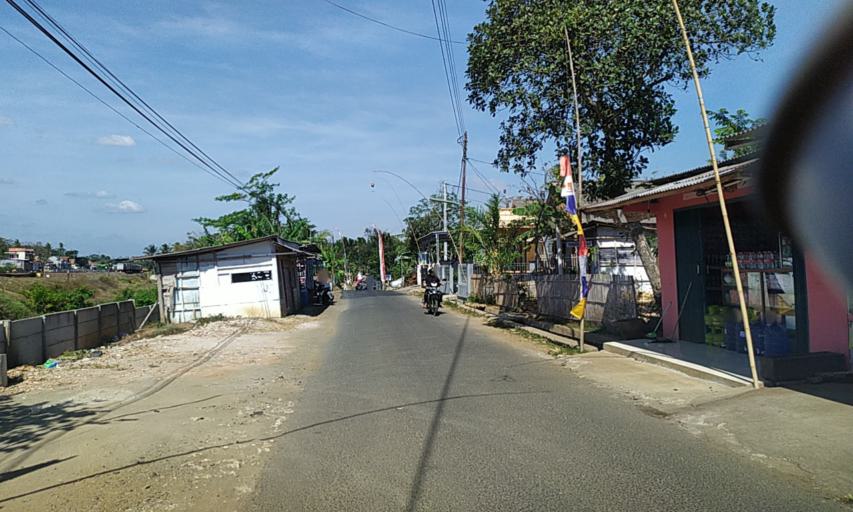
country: ID
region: Central Java
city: Kroya
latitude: -7.6298
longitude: 109.2569
